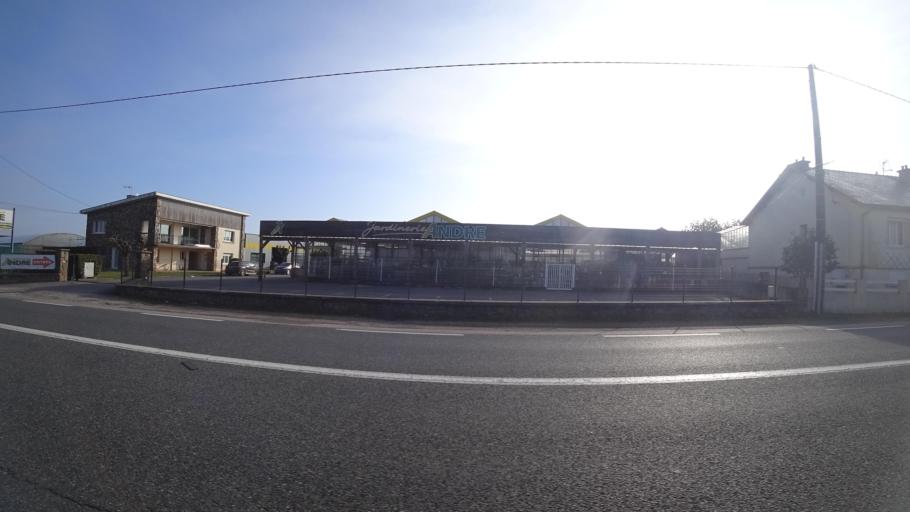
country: FR
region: Midi-Pyrenees
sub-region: Departement de l'Aveyron
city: Luc-la-Primaube
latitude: 44.3212
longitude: 2.5584
